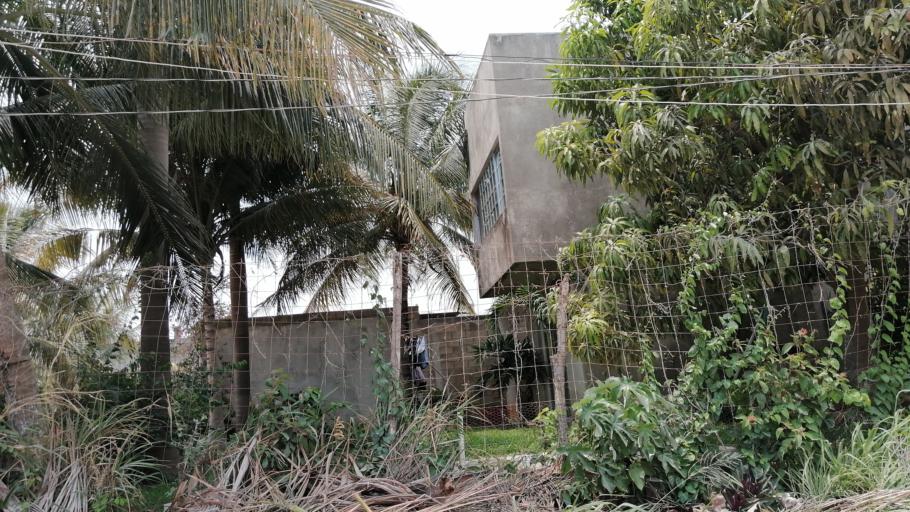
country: MX
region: Quintana Roo
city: Cancun
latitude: 21.1372
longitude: -86.8973
